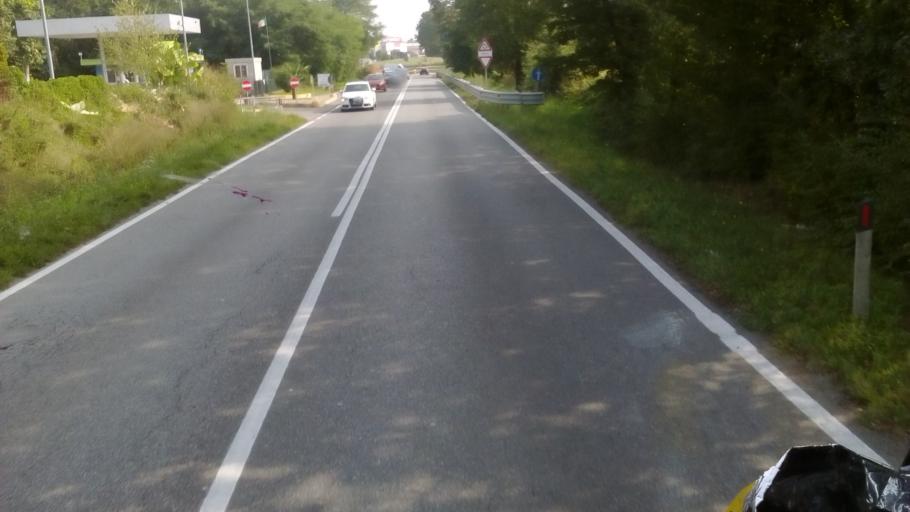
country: IT
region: Lombardy
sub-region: Provincia di Como
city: San Michele-San Giorgio
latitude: 45.6920
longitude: 9.0639
